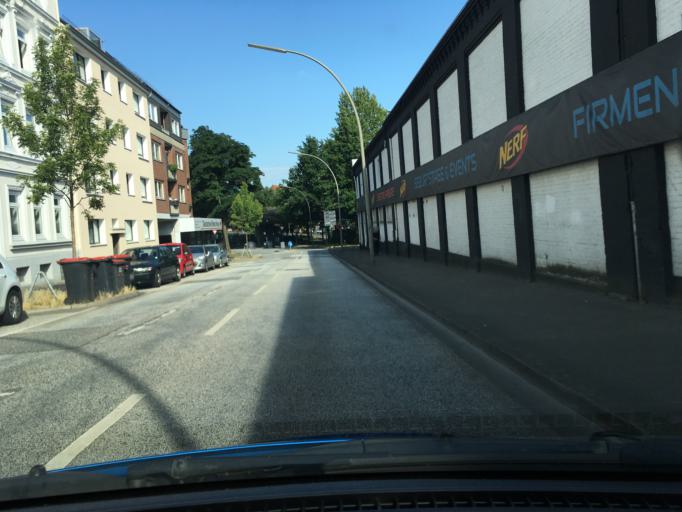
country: DE
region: Hamburg
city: Harburg
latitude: 53.4520
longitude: 9.9854
